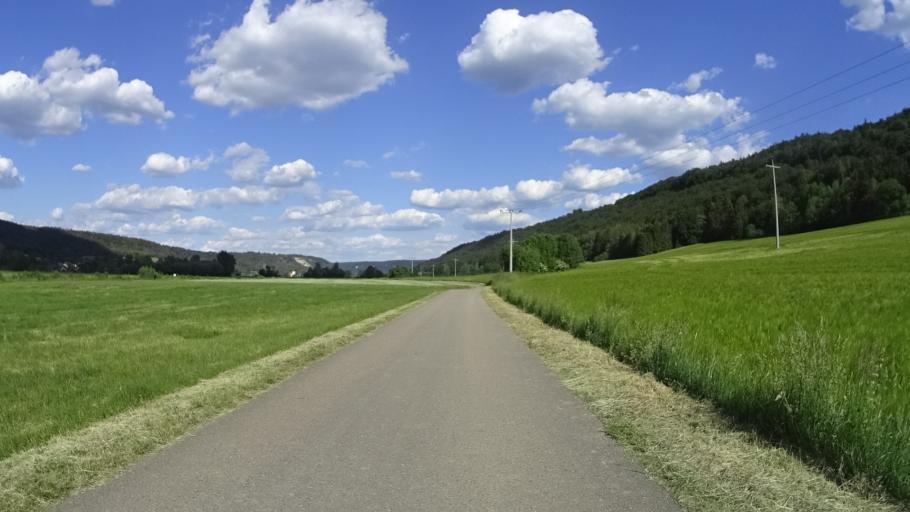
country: DE
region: Bavaria
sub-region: Upper Bavaria
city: Denkendorf
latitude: 49.0196
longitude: 11.4885
